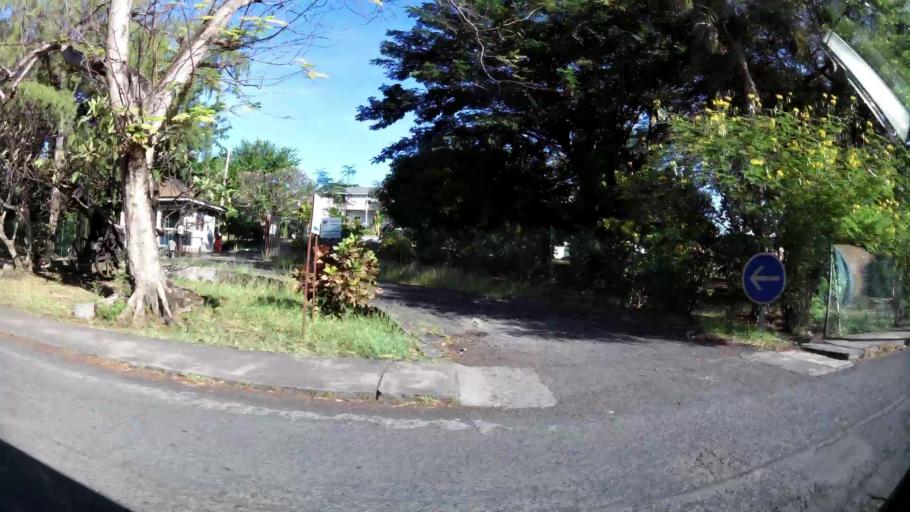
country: YT
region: Dzaoudzi
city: Dzaoudzi
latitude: -12.7818
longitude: 45.2557
